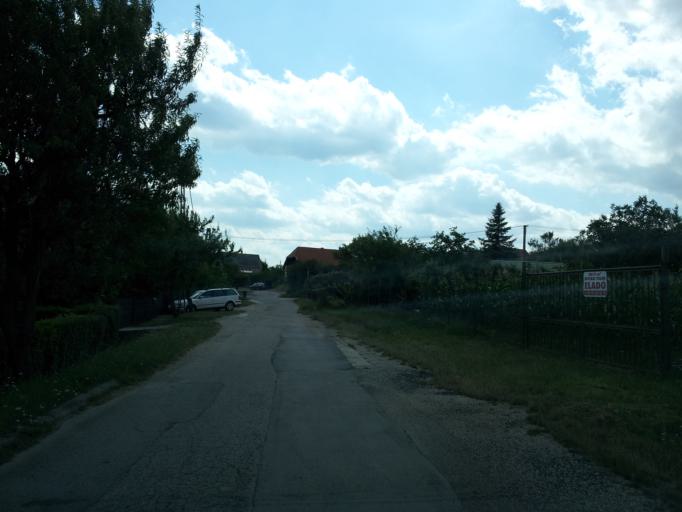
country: HU
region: Veszprem
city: Balatonalmadi
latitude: 47.0532
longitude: 18.0144
